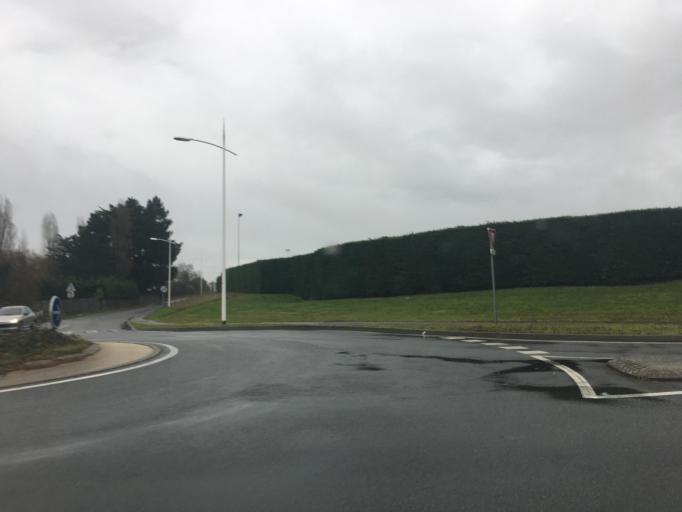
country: FR
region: Pays de la Loire
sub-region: Departement de la Loire-Atlantique
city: Guerande
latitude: 47.3299
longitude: -2.4125
